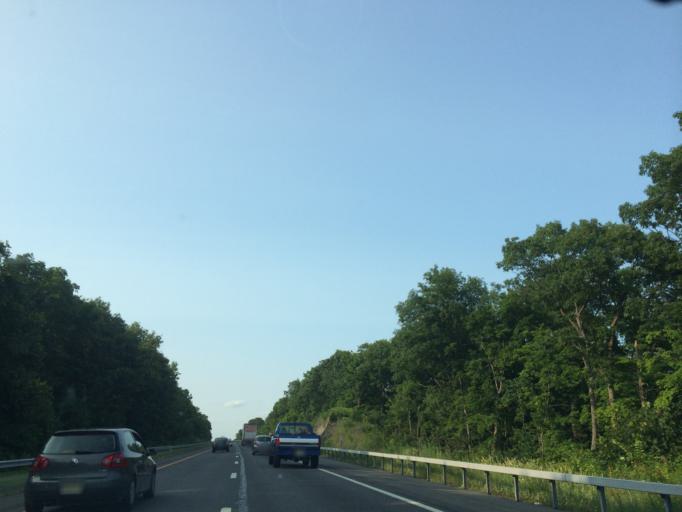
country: US
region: New York
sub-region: Greene County
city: Jefferson Heights
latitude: 42.2716
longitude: -73.8740
